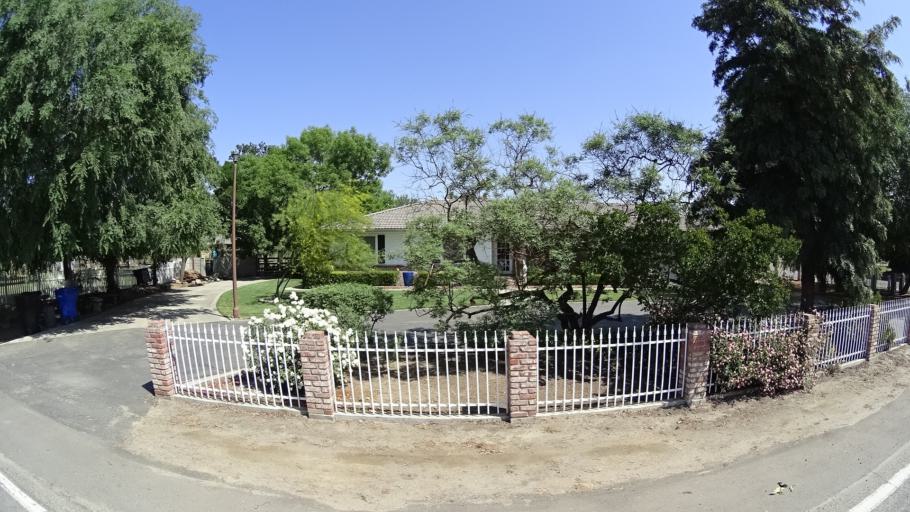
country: US
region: California
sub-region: Kings County
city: Home Garden
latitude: 36.3134
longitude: -119.6215
